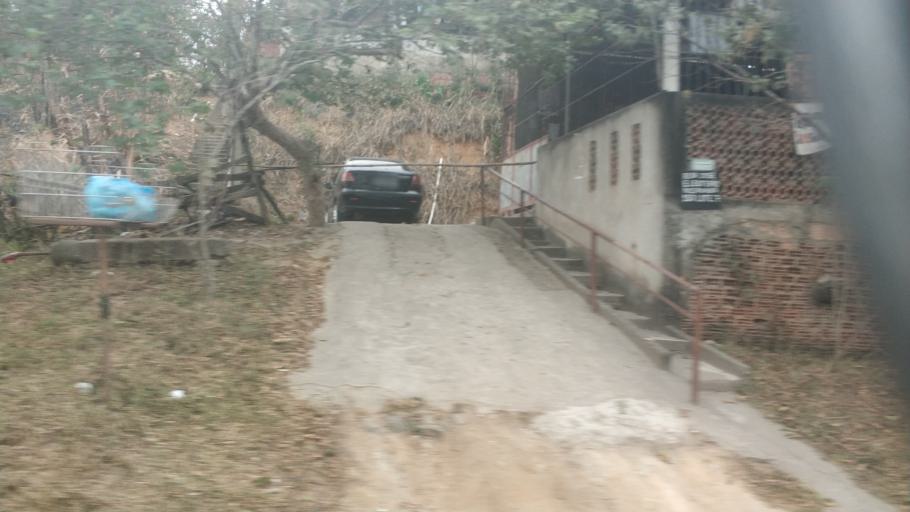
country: BR
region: Rio de Janeiro
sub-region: Seropedica
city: Seropedica
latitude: -22.8139
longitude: -43.6325
